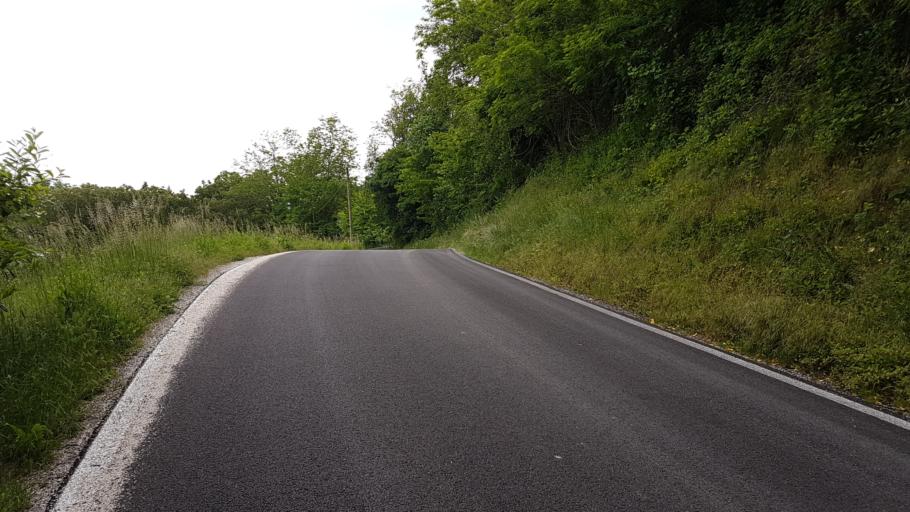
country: IT
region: Veneto
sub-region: Provincia di Vicenza
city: Nogarole Vicentino
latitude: 45.5460
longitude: 11.3148
